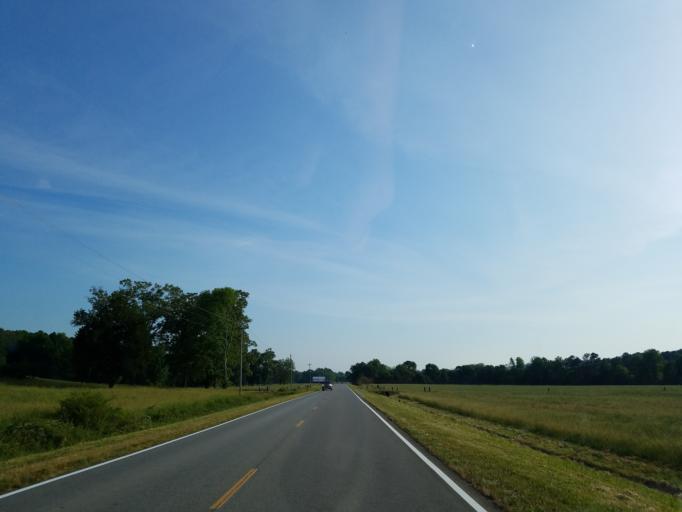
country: US
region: Georgia
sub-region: Chattooga County
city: Trion
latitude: 34.5054
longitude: -85.2411
